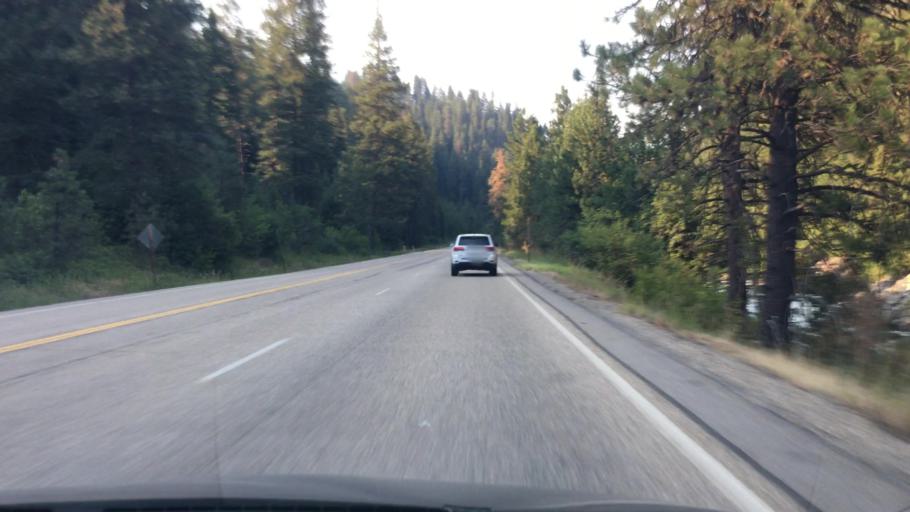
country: US
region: Idaho
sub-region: Valley County
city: Cascade
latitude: 44.1703
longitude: -116.1207
